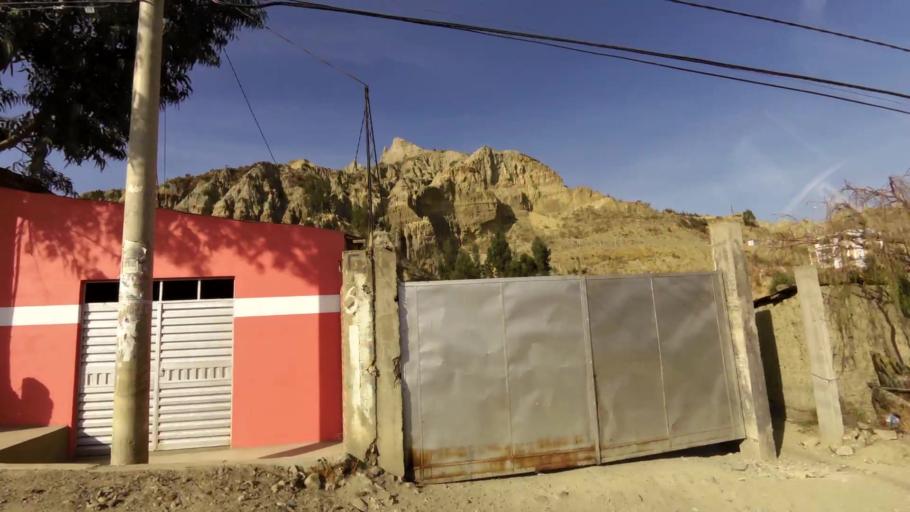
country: BO
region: La Paz
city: La Paz
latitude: -16.5008
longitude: -68.0822
